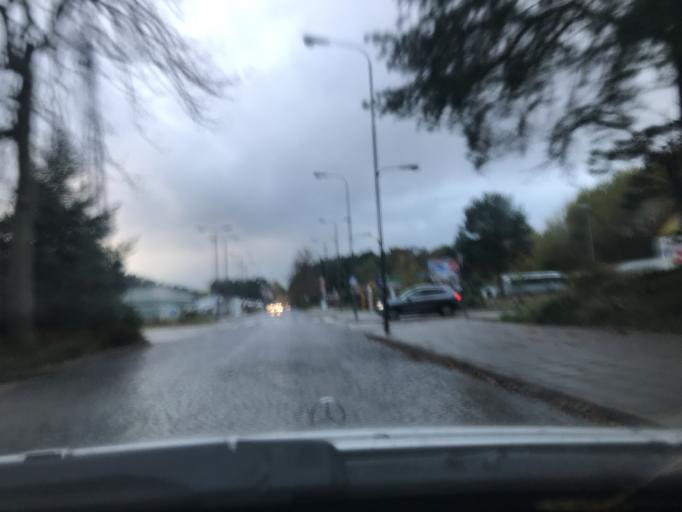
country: PL
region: West Pomeranian Voivodeship
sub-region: Swinoujscie
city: Swinoujscie
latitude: 53.9215
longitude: 14.2183
